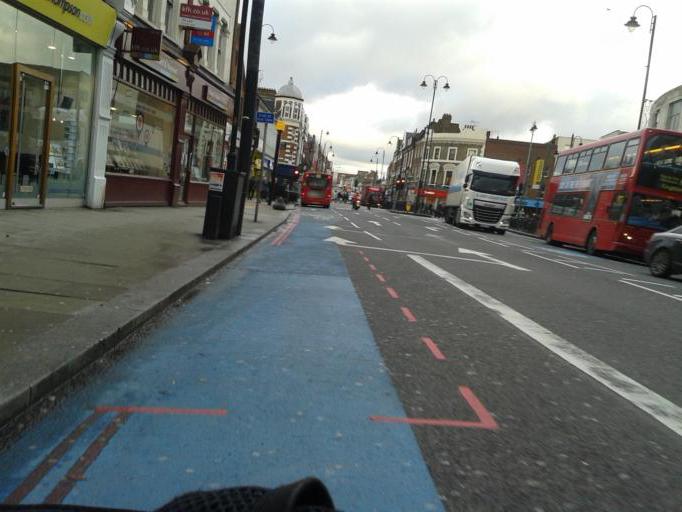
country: GB
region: England
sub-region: Greater London
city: Earlsfield
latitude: 51.4273
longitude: -0.1685
